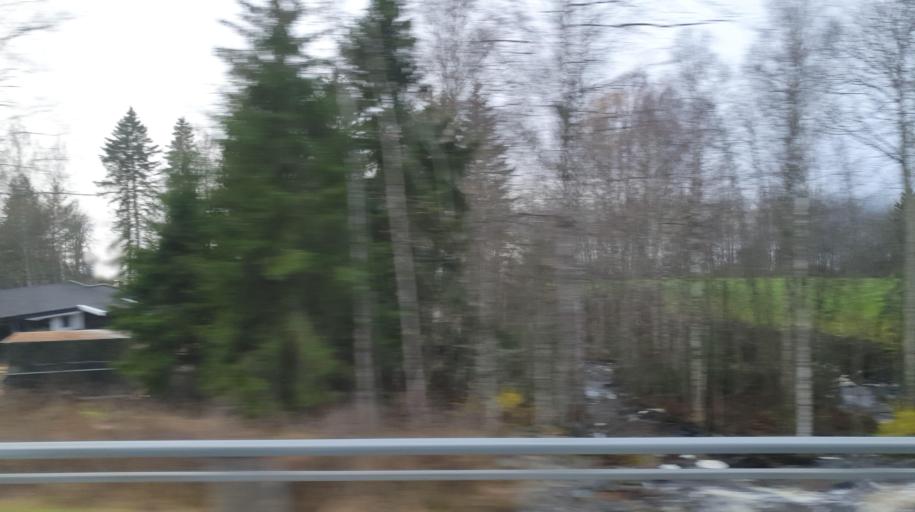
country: NO
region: Buskerud
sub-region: Krodsherad
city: Noresund
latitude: 60.1447
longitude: 9.7678
